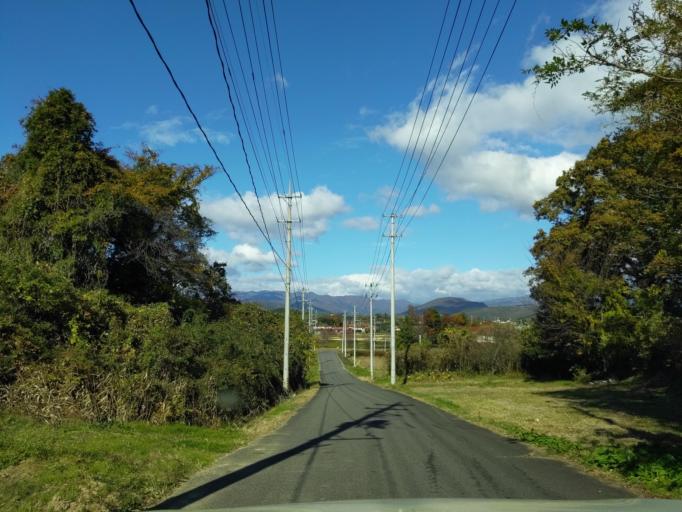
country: JP
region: Fukushima
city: Koriyama
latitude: 37.4498
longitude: 140.3219
